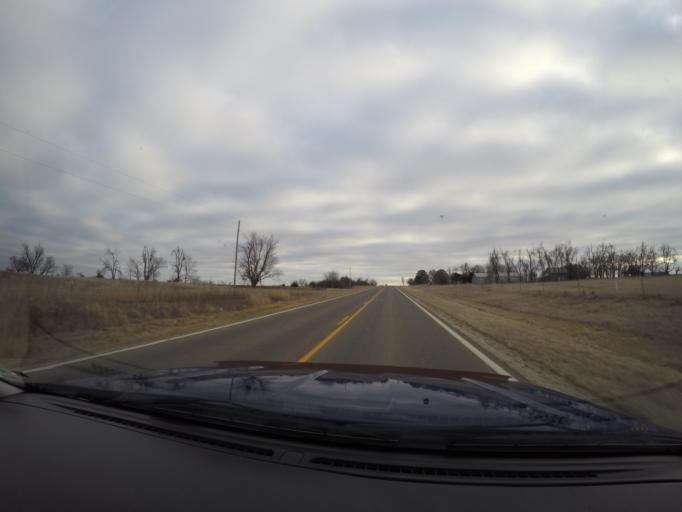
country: US
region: Kansas
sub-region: Morris County
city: Council Grove
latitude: 38.8051
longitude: -96.5013
